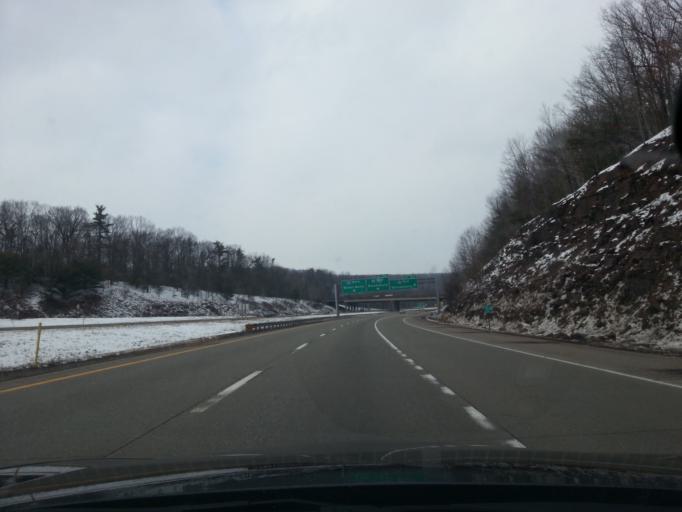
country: US
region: Pennsylvania
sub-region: Luzerne County
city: Conyngham
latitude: 41.0421
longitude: -76.0145
